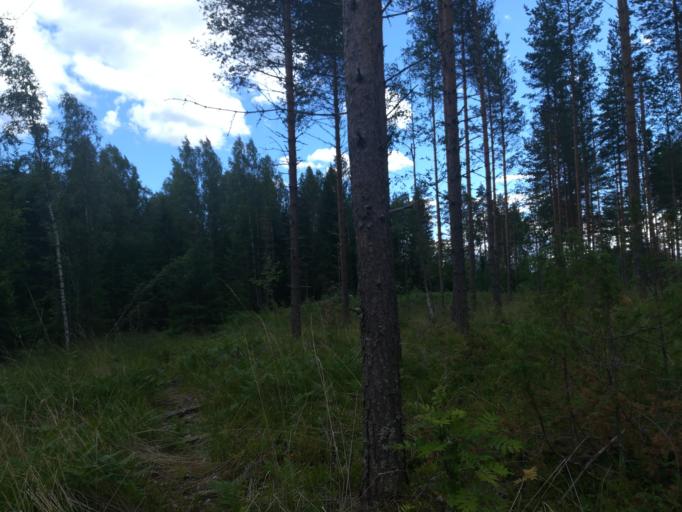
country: FI
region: Southern Savonia
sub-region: Mikkeli
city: Hirvensalmi
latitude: 61.7058
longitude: 26.9723
